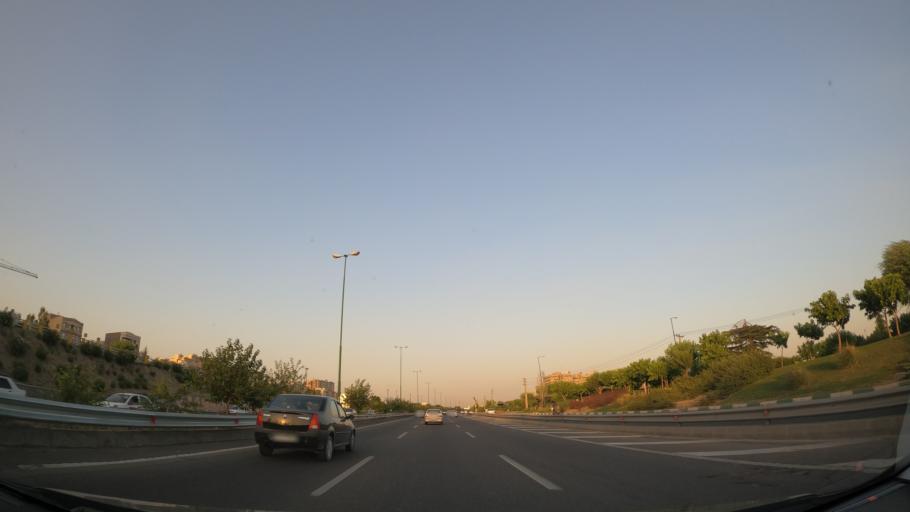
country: IR
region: Tehran
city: Tehran
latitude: 35.7170
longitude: 51.3095
